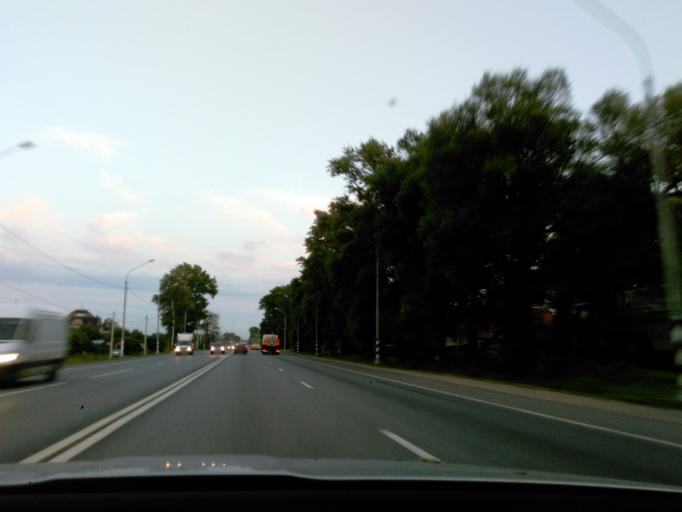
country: RU
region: Moskovskaya
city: Klin
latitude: 56.3580
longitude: 36.6963
